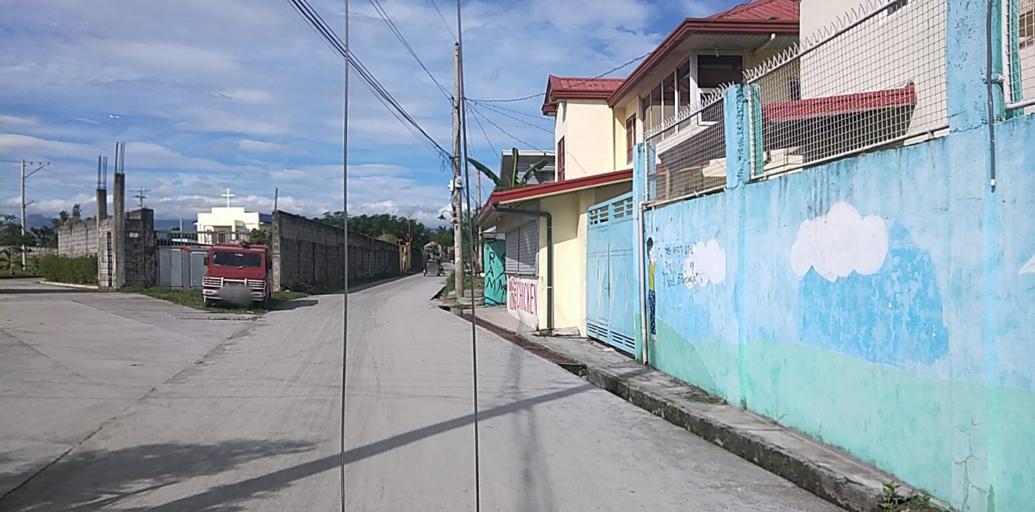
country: PH
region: Central Luzon
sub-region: Province of Pampanga
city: Angeles City
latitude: 15.1297
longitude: 120.5596
